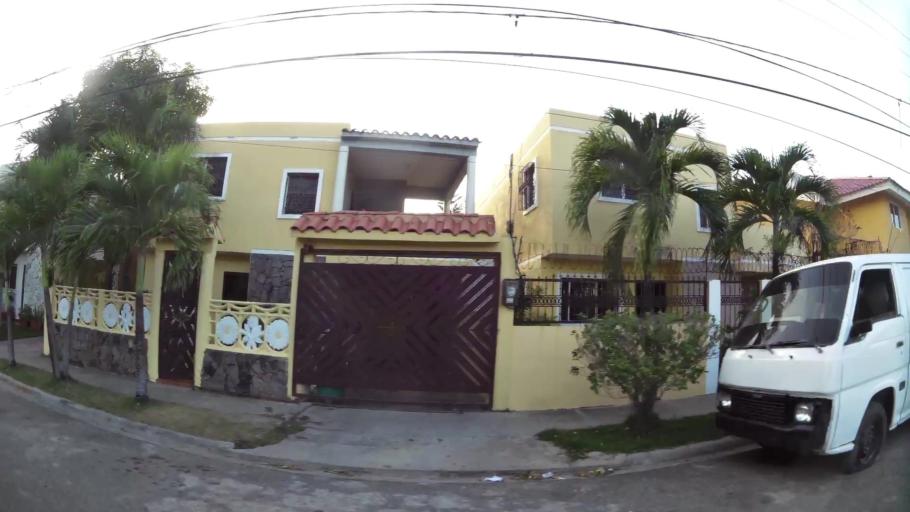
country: DO
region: Nacional
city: La Agustina
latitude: 18.5455
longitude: -69.9215
